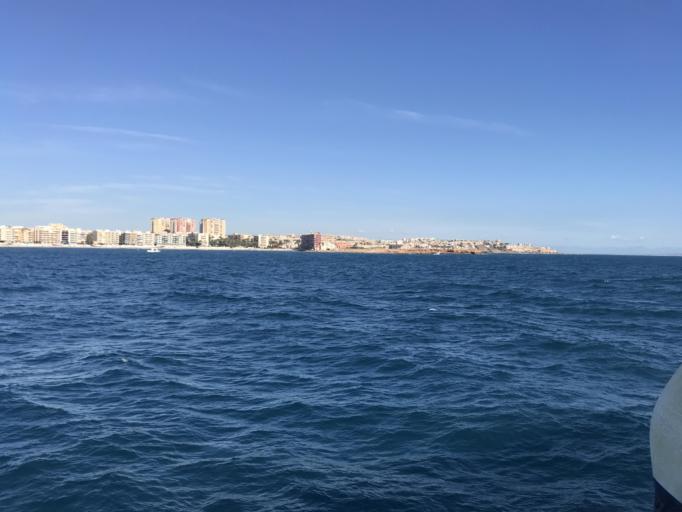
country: ES
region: Valencia
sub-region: Provincia de Alicante
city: Torrevieja
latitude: 37.9764
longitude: -0.6560
